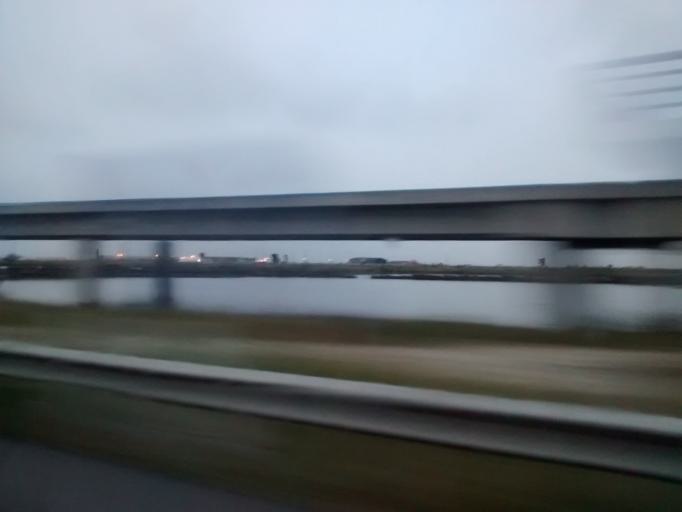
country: PT
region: Aveiro
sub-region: Aveiro
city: Aveiro
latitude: 40.6460
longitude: -8.6549
